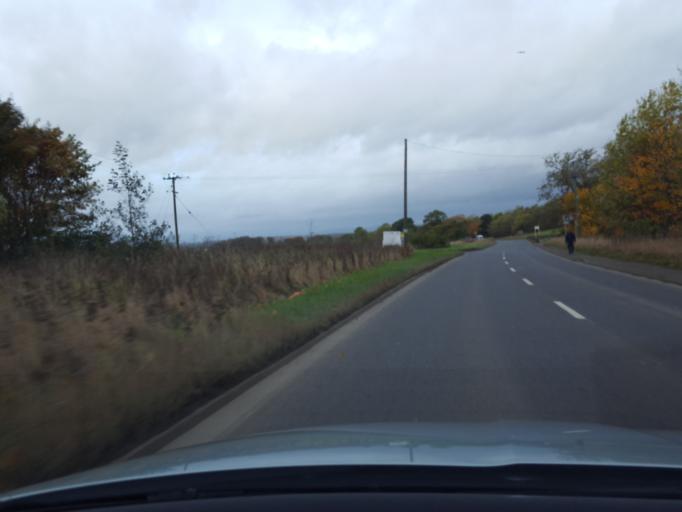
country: GB
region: Scotland
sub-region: Edinburgh
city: Newbridge
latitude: 55.9155
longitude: -3.4087
